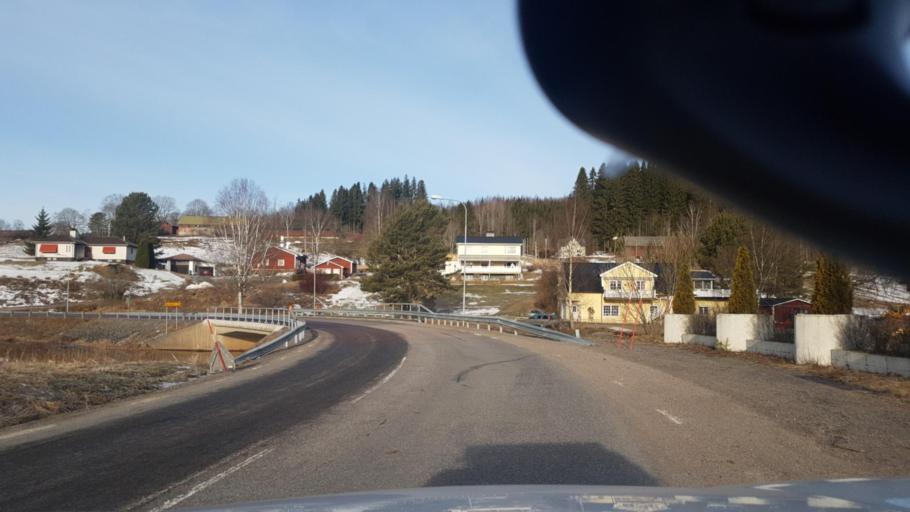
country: SE
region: Vaermland
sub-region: Eda Kommun
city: Amotfors
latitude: 59.8861
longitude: 12.5231
